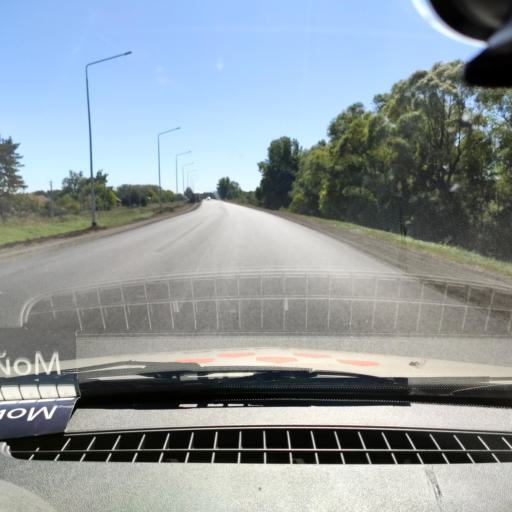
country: RU
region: Bashkortostan
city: Yermolayevo
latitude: 52.6624
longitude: 55.8331
